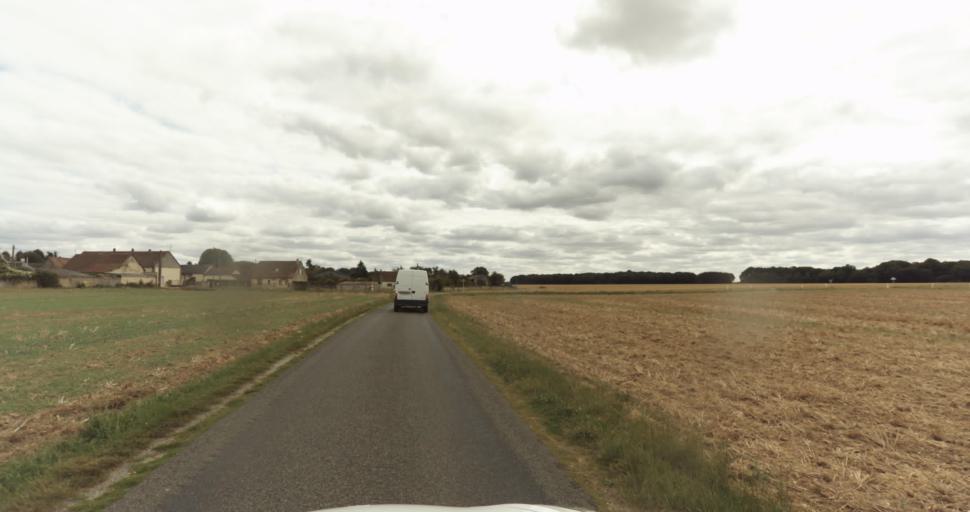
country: FR
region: Haute-Normandie
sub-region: Departement de l'Eure
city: Saint-Germain-sur-Avre
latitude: 48.8024
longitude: 1.2594
